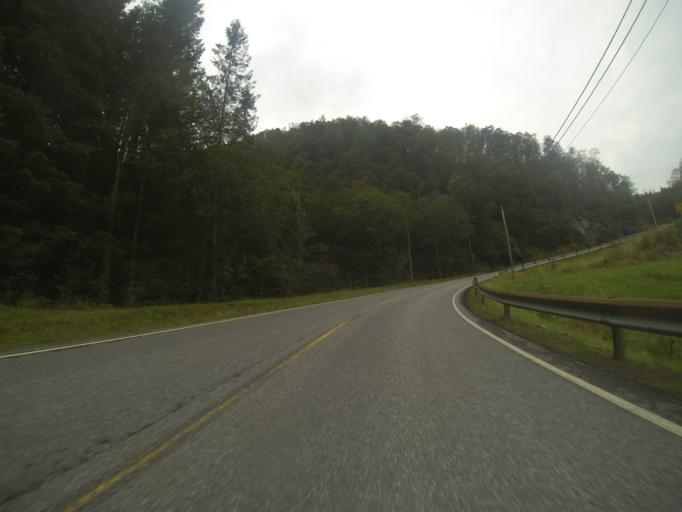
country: NO
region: Rogaland
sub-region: Suldal
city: Sand
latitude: 59.4844
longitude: 6.2051
